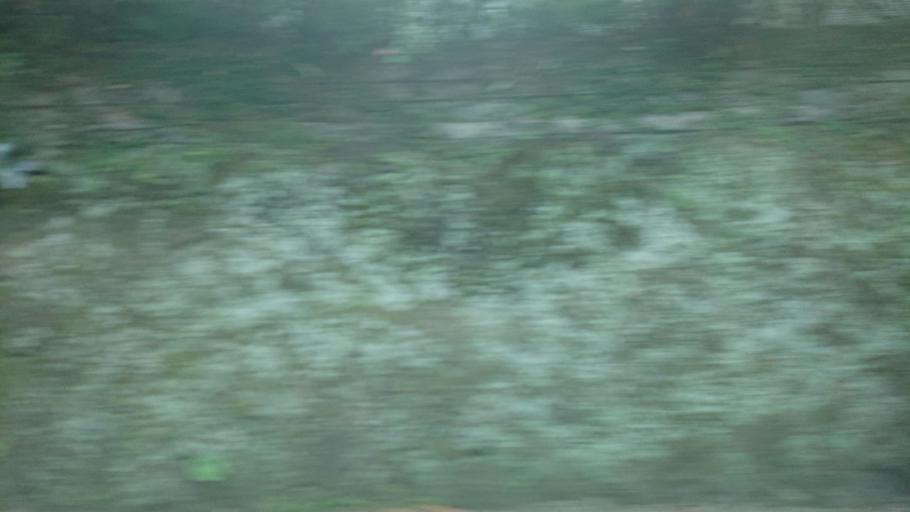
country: TW
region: Taiwan
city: Daxi
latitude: 24.8723
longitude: 121.4047
